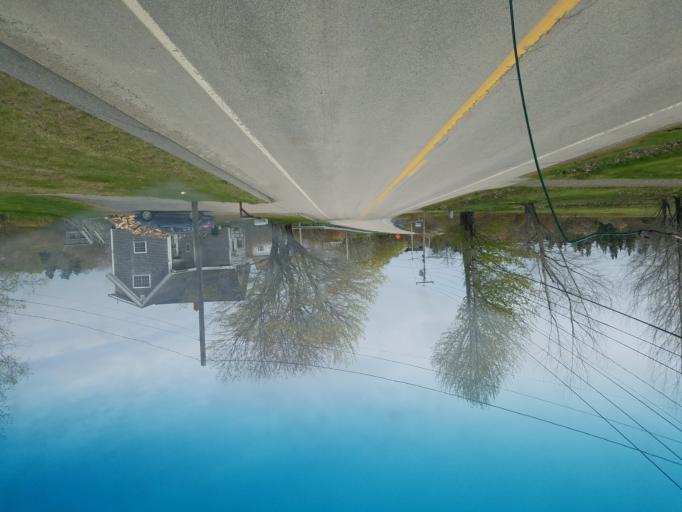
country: US
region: Maine
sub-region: Washington County
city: Eastport
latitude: 44.7898
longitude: -67.1694
